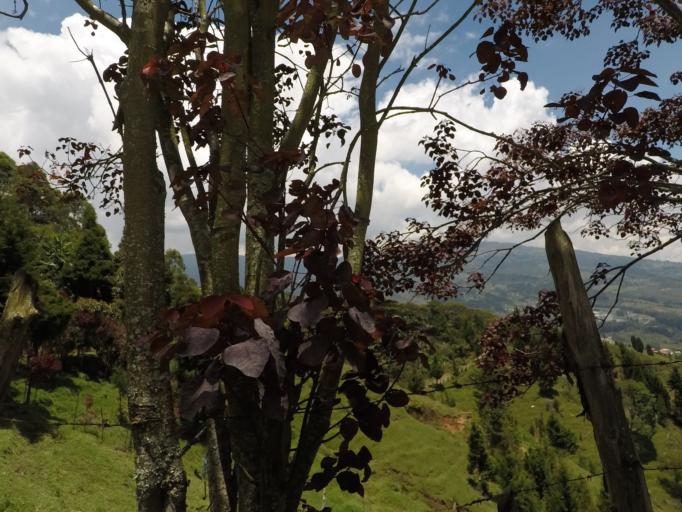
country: CO
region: Antioquia
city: Medellin
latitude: 6.2658
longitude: -75.6425
